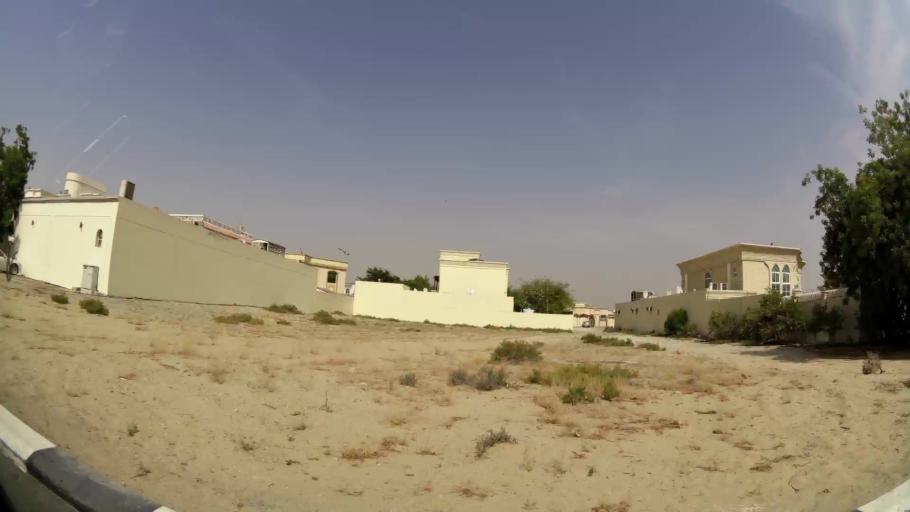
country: AE
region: Ash Shariqah
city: Sharjah
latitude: 25.2508
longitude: 55.4416
